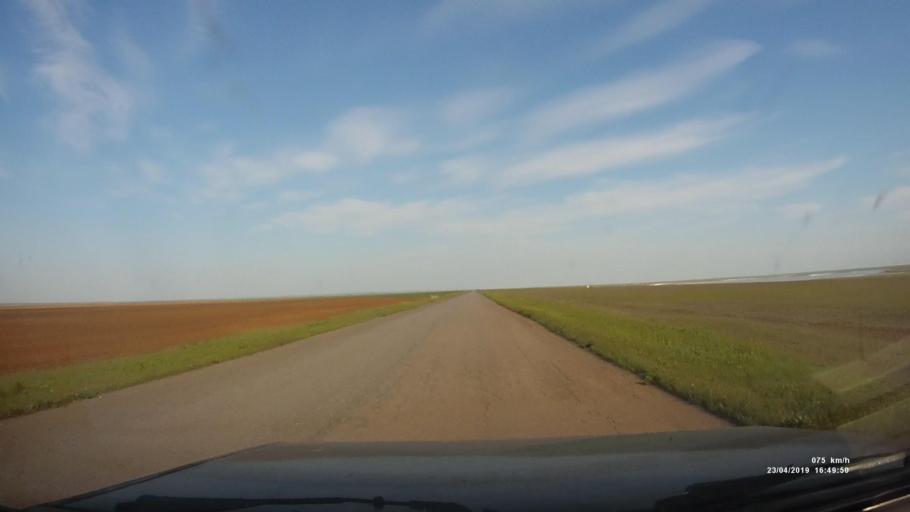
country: RU
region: Kalmykiya
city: Priyutnoye
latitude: 46.3294
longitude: 43.2825
